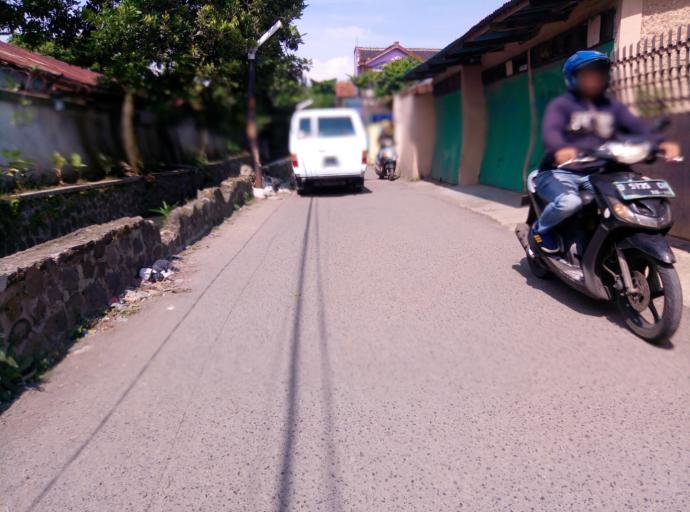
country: ID
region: West Java
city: Bandung
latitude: -6.9320
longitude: 107.6457
